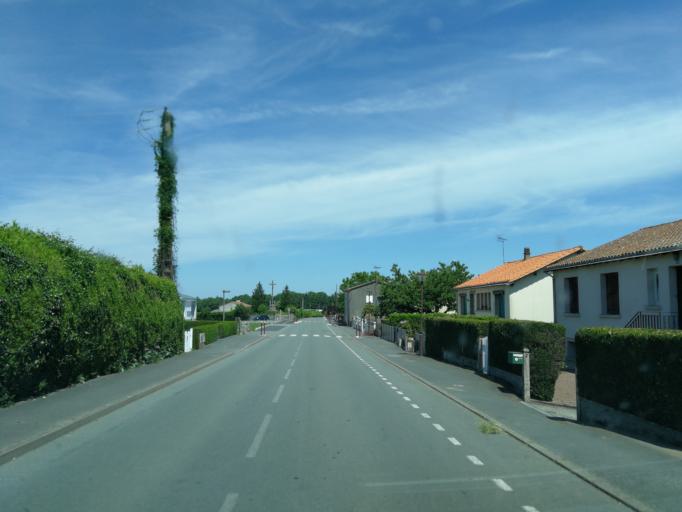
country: FR
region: Pays de la Loire
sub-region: Departement de la Vendee
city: Saint-Pierre-du-Chemin
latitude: 46.6975
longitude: -0.6974
